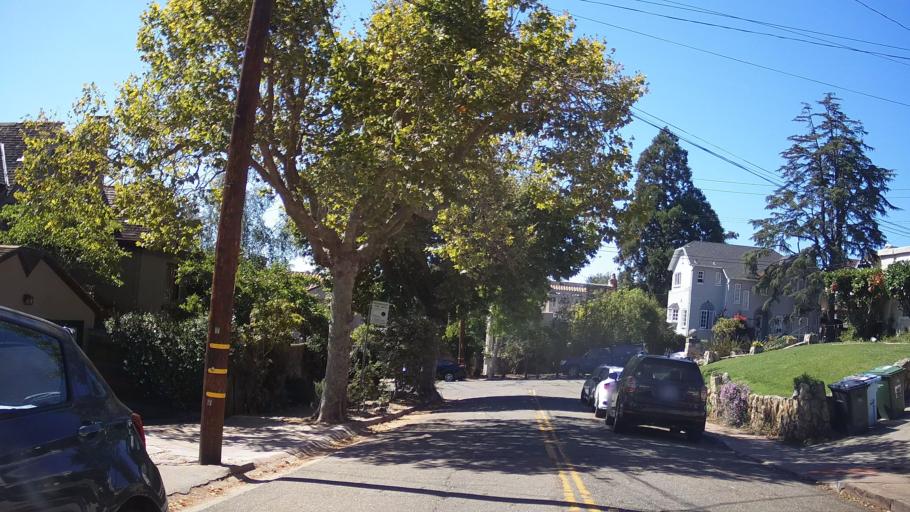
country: US
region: California
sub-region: Contra Costa County
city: Kensington
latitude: 37.8927
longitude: -122.2722
